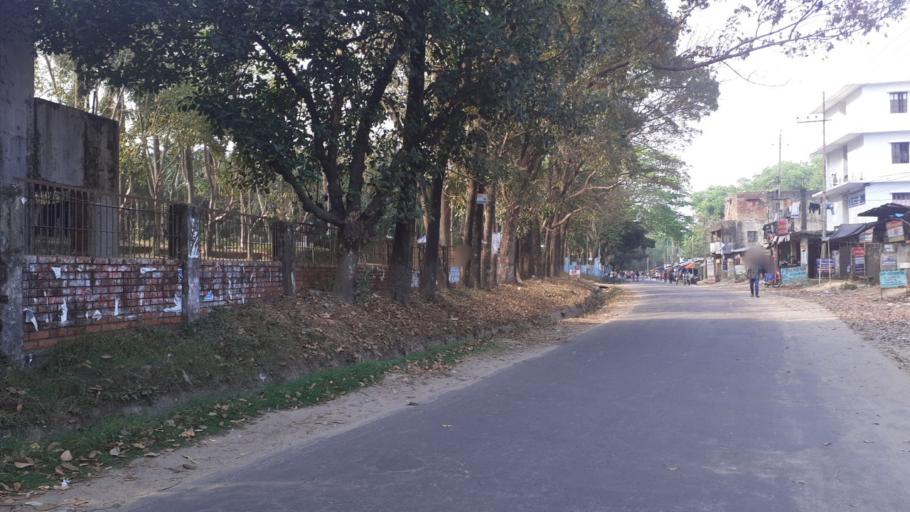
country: BD
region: Chittagong
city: Chittagong
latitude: 22.4722
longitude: 91.7933
